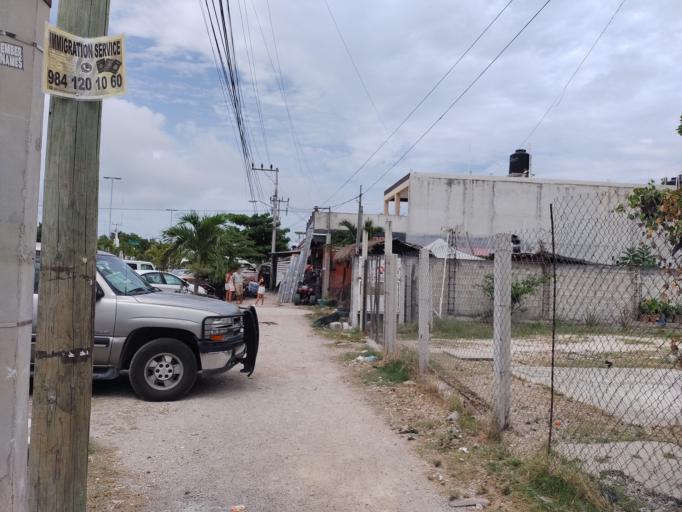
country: MX
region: Quintana Roo
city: Tulum
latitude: 20.2084
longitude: -87.4709
